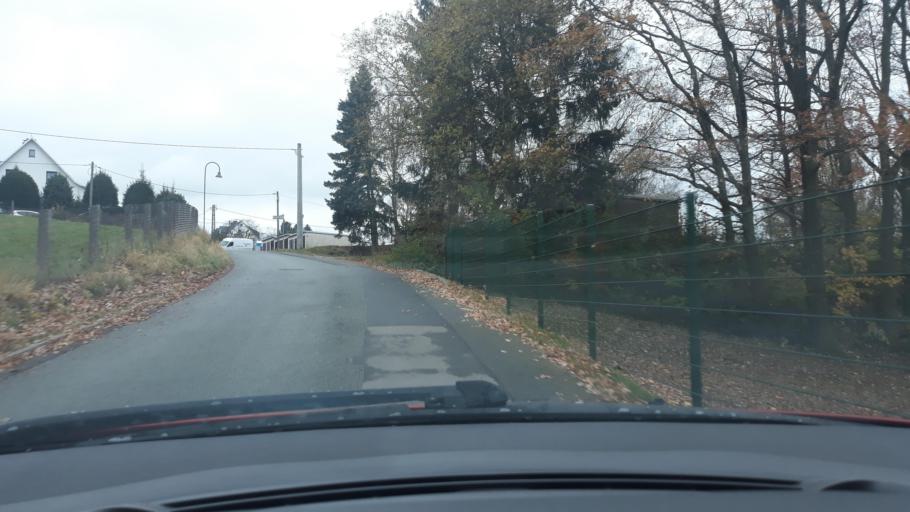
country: DE
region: Saxony
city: Kirchberg
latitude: 50.6167
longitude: 12.5234
